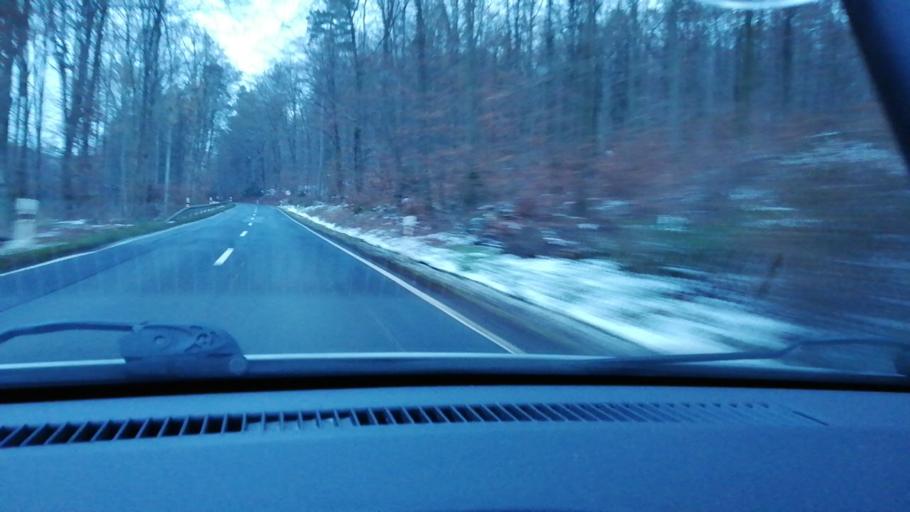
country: DE
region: Bavaria
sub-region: Regierungsbezirk Unterfranken
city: Geiselbach
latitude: 50.1362
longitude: 9.1715
